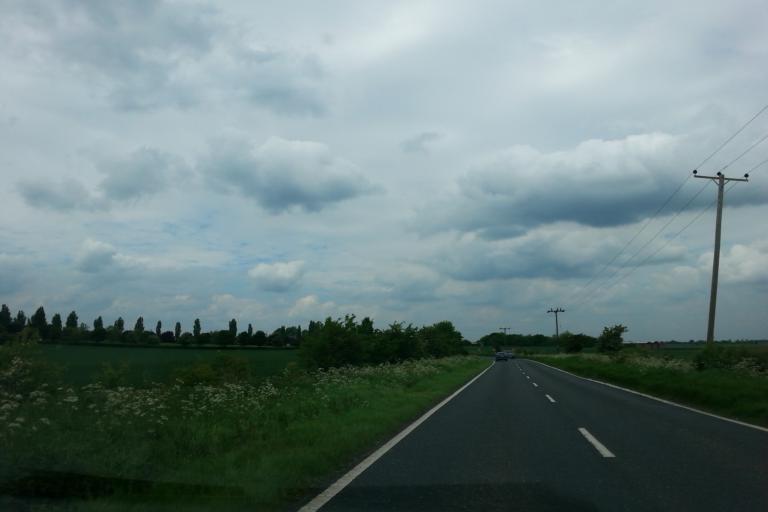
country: GB
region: England
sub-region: Cambridgeshire
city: Ramsey
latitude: 52.4257
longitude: -0.1048
